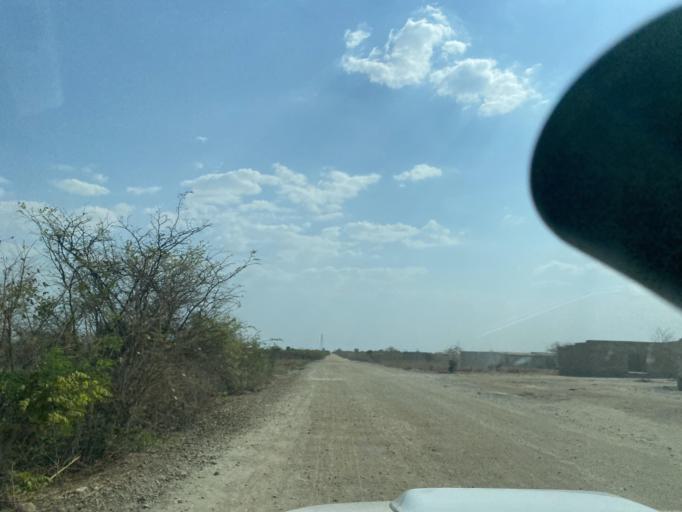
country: ZM
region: Lusaka
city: Lusaka
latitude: -15.3620
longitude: 28.0917
